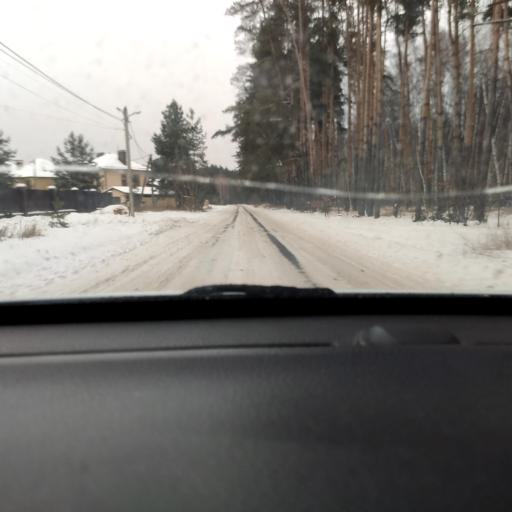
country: RU
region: Voronezj
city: Somovo
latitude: 51.7097
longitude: 39.3211
